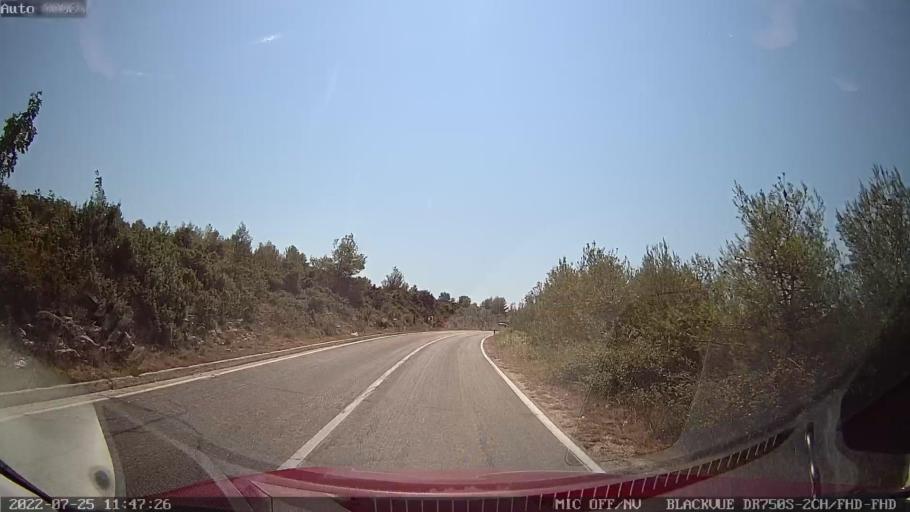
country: HR
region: Zadarska
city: Razanac
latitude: 44.2385
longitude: 15.3017
